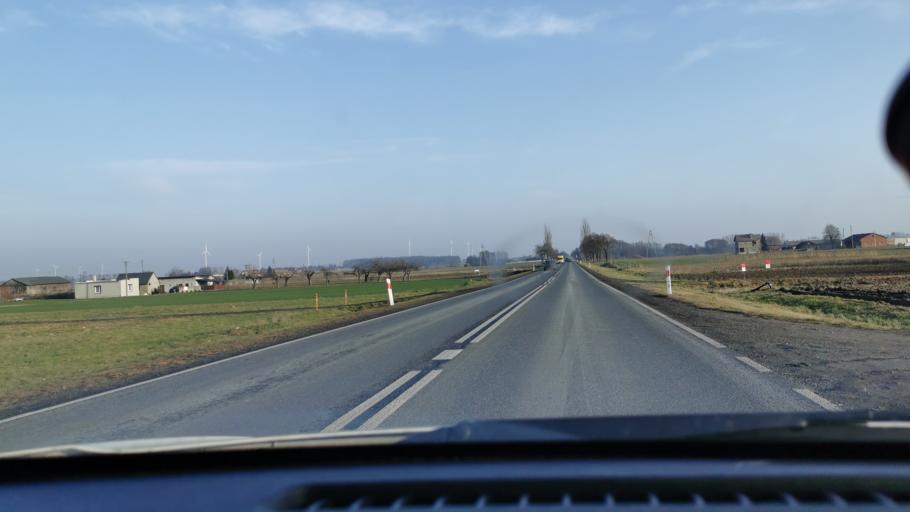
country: PL
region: Lodz Voivodeship
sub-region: Powiat sieradzki
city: Blaszki
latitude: 51.6436
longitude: 18.4842
